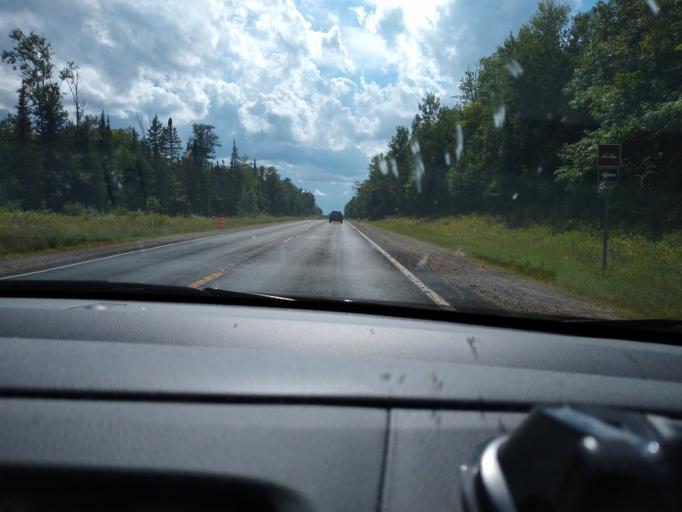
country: US
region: Michigan
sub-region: Marquette County
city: West Ishpeming
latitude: 46.3052
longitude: -87.9881
